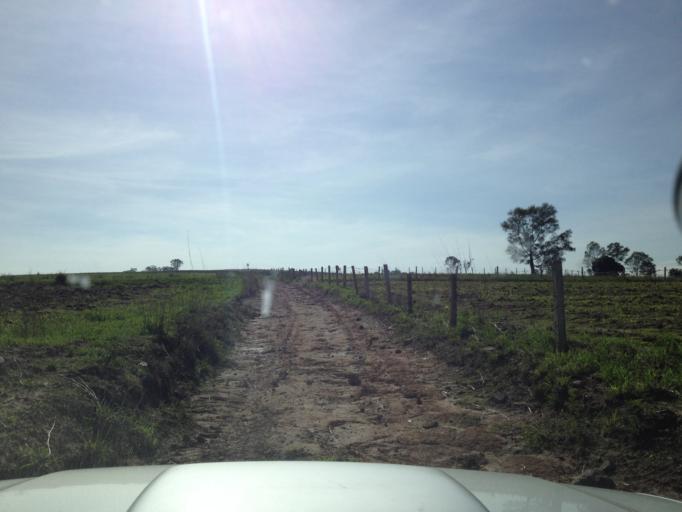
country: MX
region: Michoacan
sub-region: Tarimbaro
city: Pena del Panal
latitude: 19.7680
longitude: -101.1890
